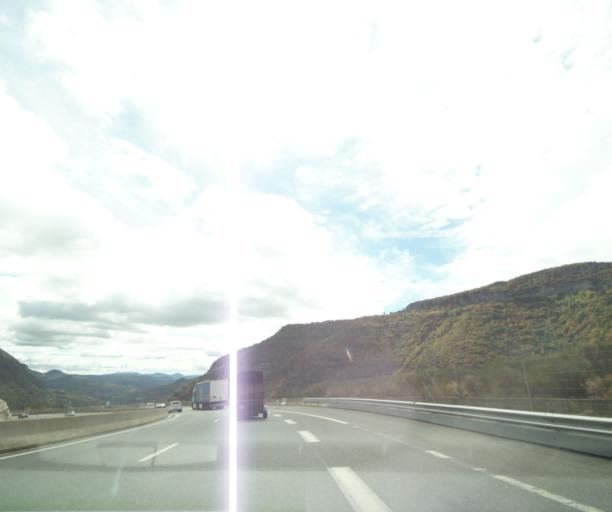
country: FR
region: Languedoc-Roussillon
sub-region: Departement de l'Herault
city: Lodeve
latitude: 43.8135
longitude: 3.3198
